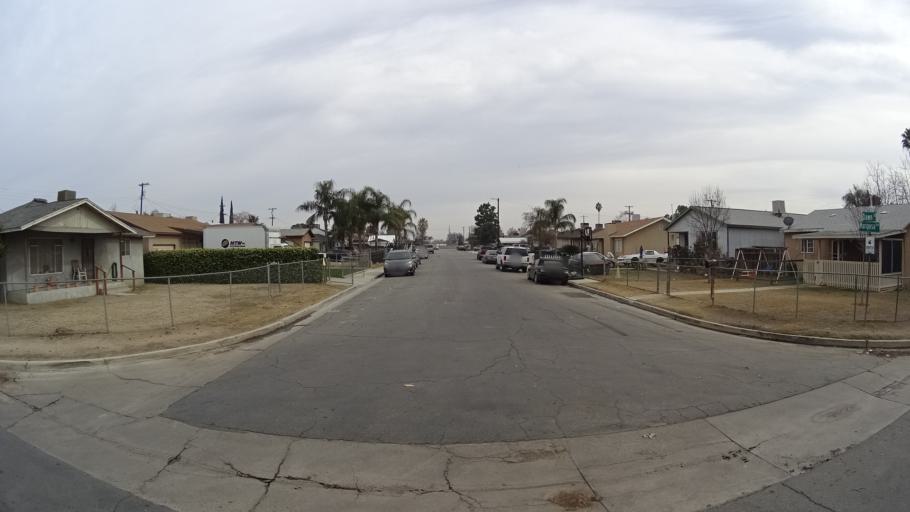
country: US
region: California
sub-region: Kern County
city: Bakersfield
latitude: 35.3438
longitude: -119.0069
